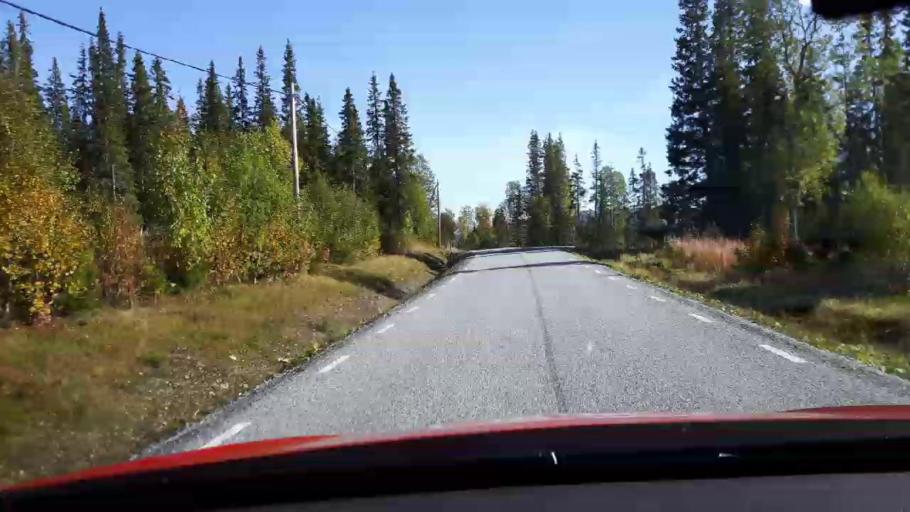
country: NO
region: Nord-Trondelag
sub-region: Royrvik
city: Royrvik
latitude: 64.8134
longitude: 14.1560
